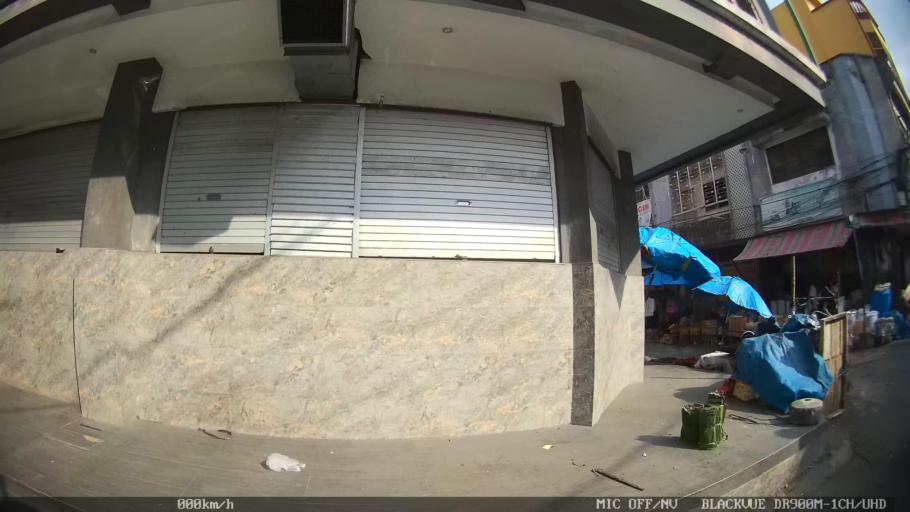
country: ID
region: North Sumatra
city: Binjai
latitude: 3.6093
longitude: 98.4896
